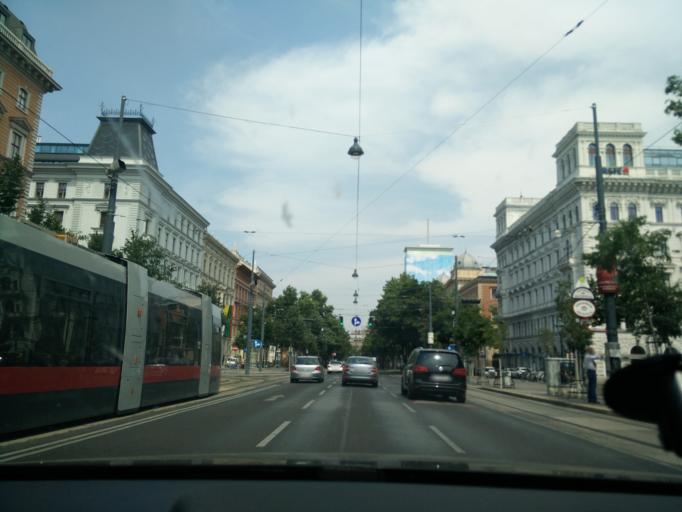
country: AT
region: Vienna
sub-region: Wien Stadt
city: Vienna
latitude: 48.2156
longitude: 16.3662
